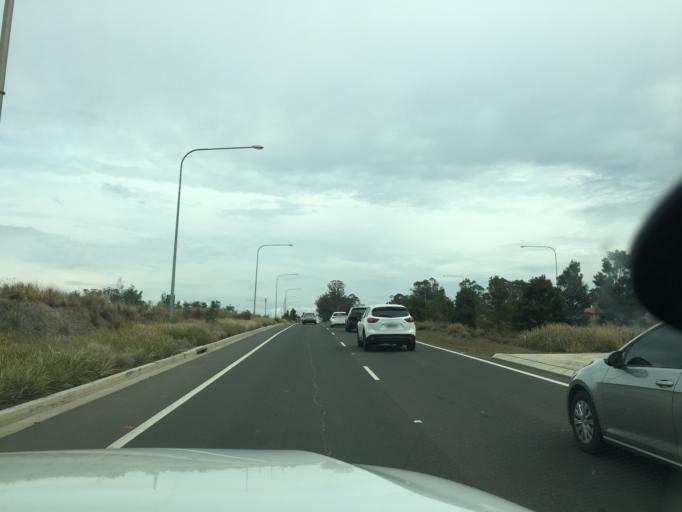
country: AU
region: New South Wales
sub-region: Campbelltown Municipality
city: Denham Court
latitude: -33.9831
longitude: 150.7981
